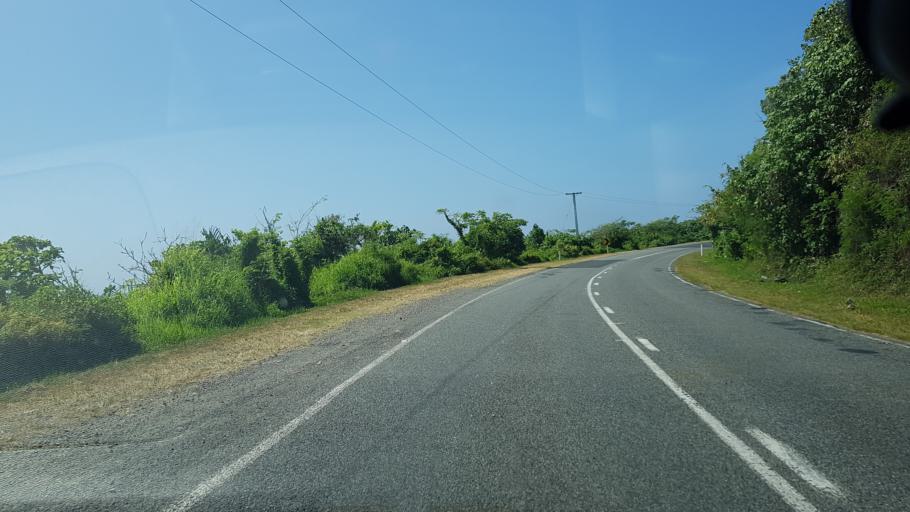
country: FJ
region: Western
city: Nadi
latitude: -18.1805
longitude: 177.5860
